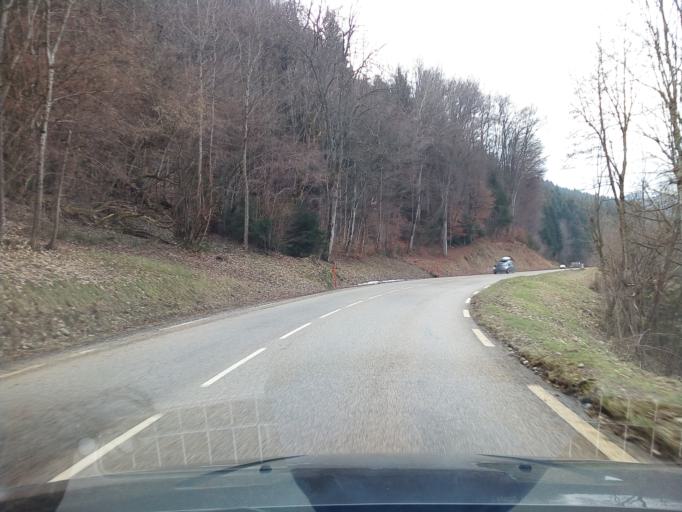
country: FR
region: Rhone-Alpes
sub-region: Departement de l'Isere
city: Revel
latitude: 45.1463
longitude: 5.8623
